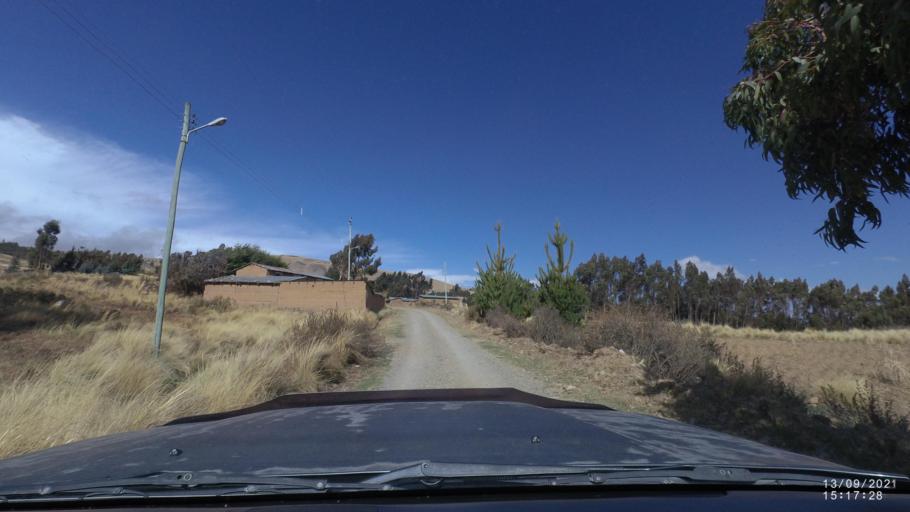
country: BO
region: Cochabamba
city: Colomi
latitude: -17.3667
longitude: -65.7887
